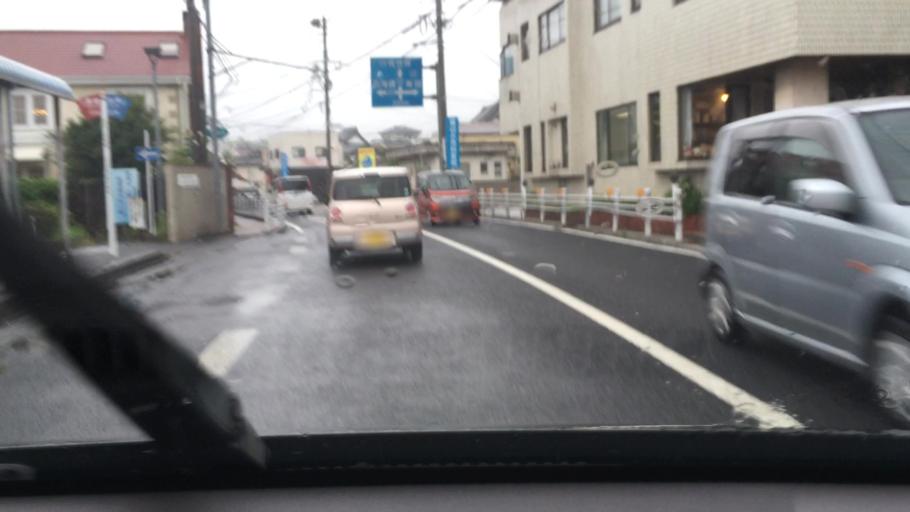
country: JP
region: Nagasaki
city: Sasebo
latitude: 33.1369
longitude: 129.7979
